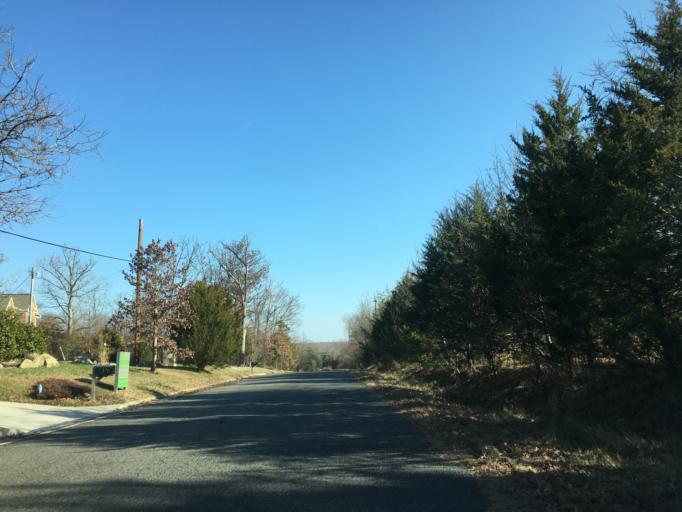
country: US
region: Virginia
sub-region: Fairfax County
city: Fairfax Station
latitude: 38.8249
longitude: -77.3705
